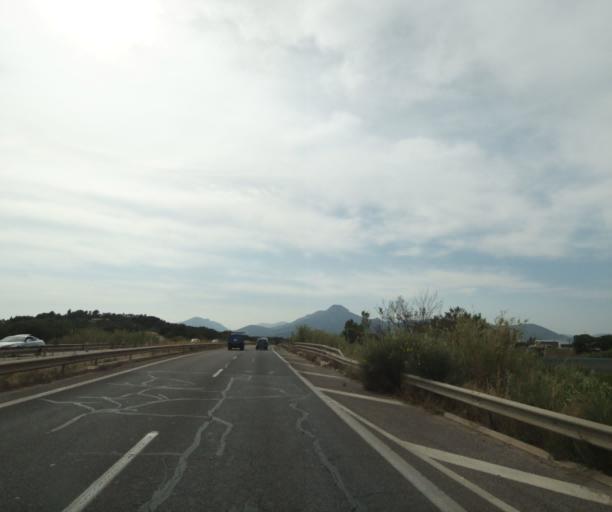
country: FR
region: Provence-Alpes-Cote d'Azur
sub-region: Departement du Var
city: La Crau
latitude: 43.1271
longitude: 6.0776
